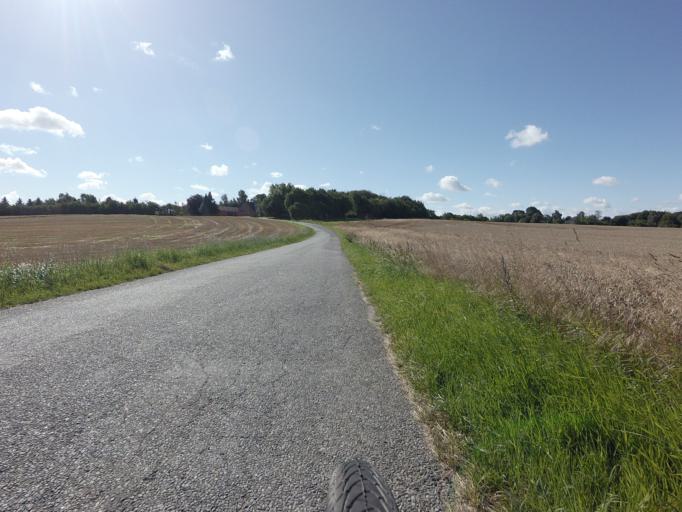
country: DK
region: Central Jutland
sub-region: Horsens Kommune
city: Braedstrup
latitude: 55.9720
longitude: 9.7127
